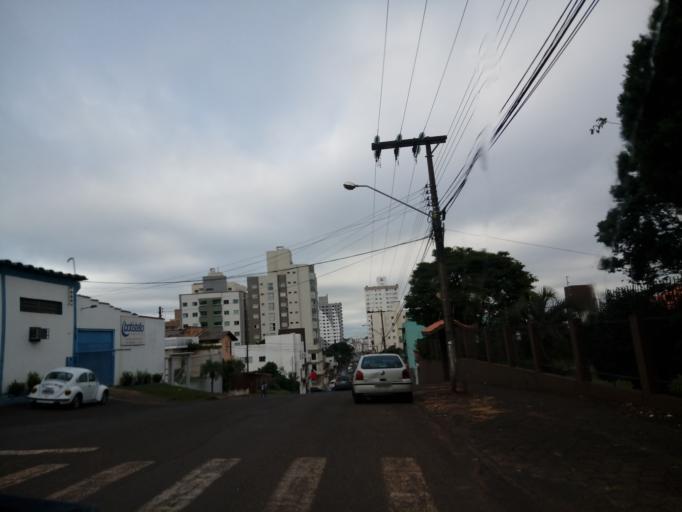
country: BR
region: Santa Catarina
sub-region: Chapeco
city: Chapeco
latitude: -27.0900
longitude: -52.6104
